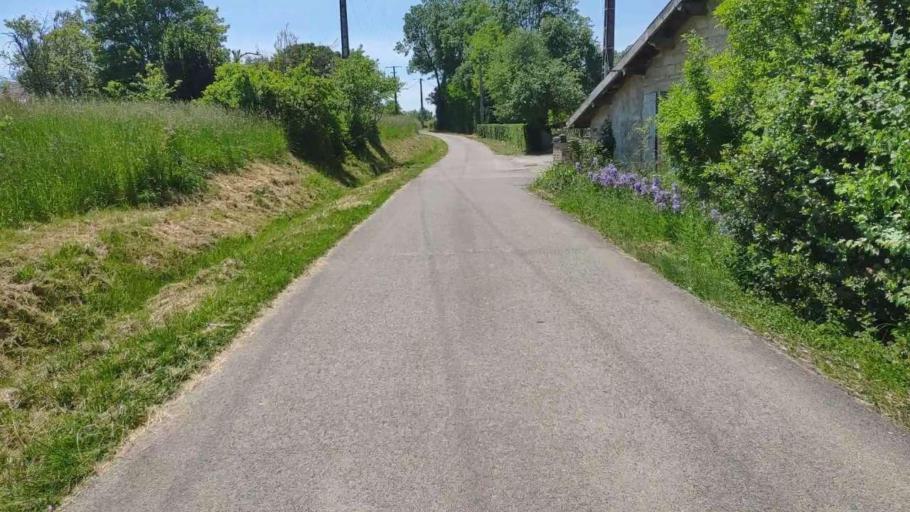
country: FR
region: Franche-Comte
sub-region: Departement du Jura
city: Bletterans
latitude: 46.7405
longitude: 5.4332
